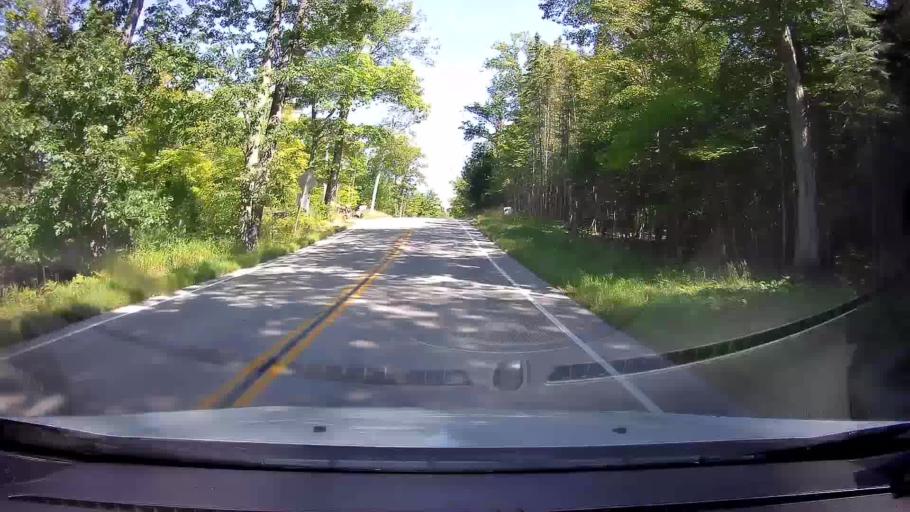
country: US
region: Michigan
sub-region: Delta County
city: Escanaba
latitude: 45.2892
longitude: -86.9957
